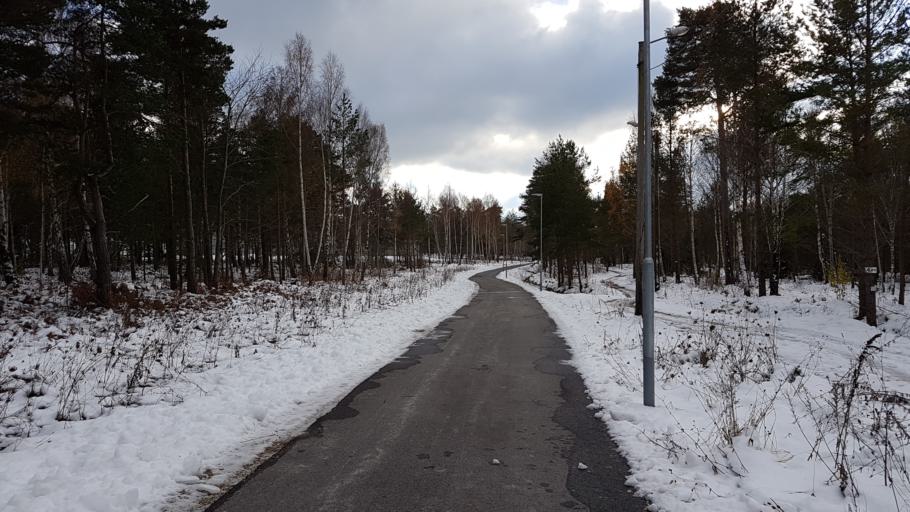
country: SE
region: Gotland
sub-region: Gotland
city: Vibble
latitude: 57.6087
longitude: 18.2805
